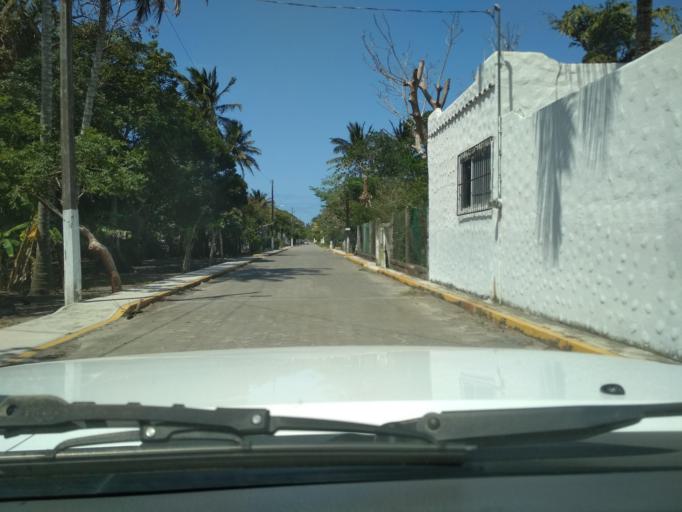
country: MX
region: Veracruz
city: Anton Lizardo
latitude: 19.0148
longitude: -95.9675
